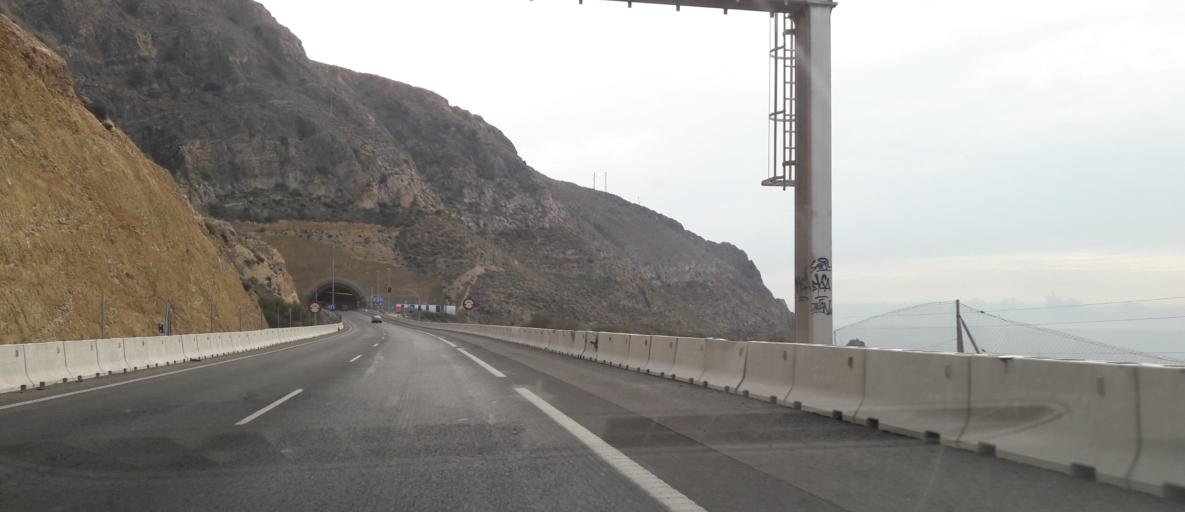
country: ES
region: Andalusia
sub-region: Provincia de Almeria
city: Aguadulce
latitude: 36.8209
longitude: -2.5672
